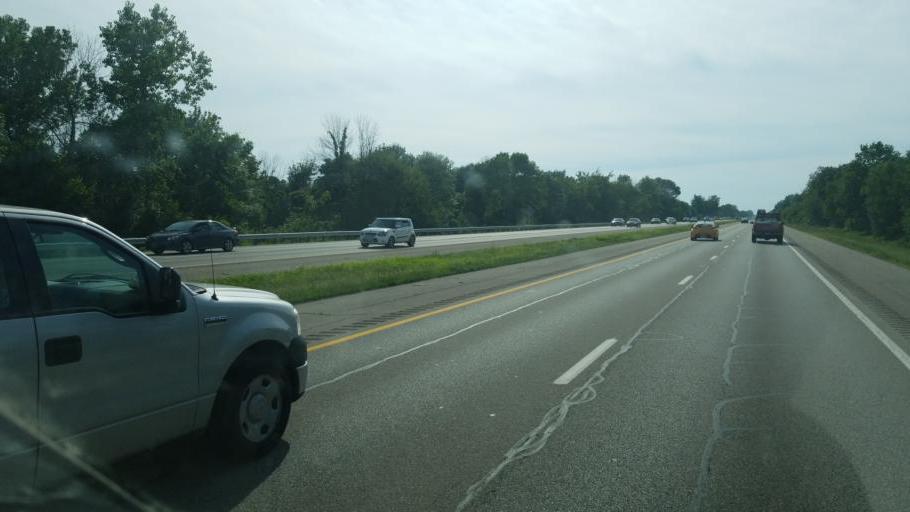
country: US
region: Ohio
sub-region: Fairfield County
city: Pickerington
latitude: 39.8305
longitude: -82.7282
